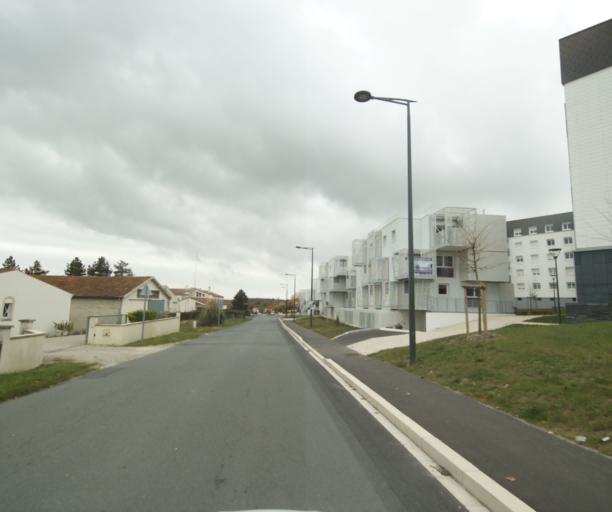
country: FR
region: Poitou-Charentes
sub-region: Departement de la Charente-Maritime
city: Saintes
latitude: 45.7326
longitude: -0.6474
